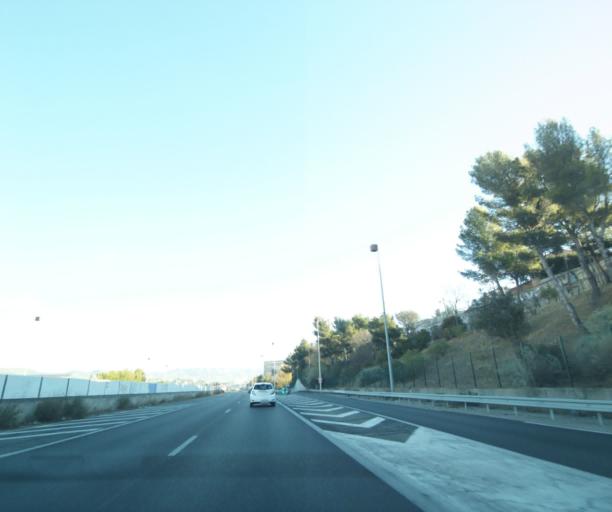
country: FR
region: Provence-Alpes-Cote d'Azur
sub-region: Departement des Bouches-du-Rhone
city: Marseille 13
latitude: 43.3182
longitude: 5.4135
